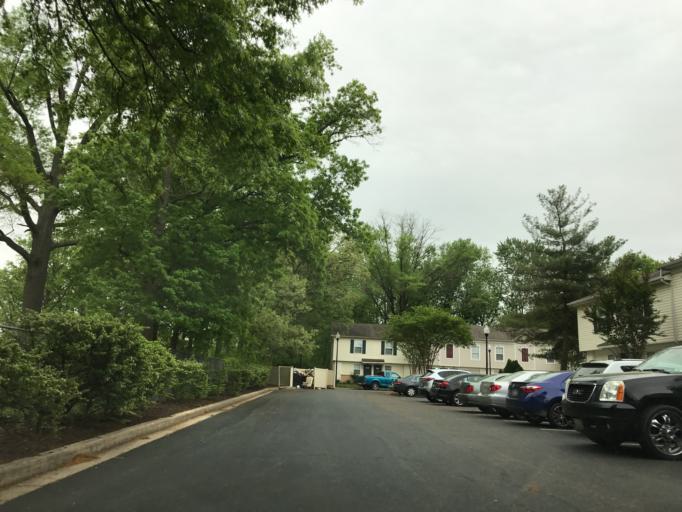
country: US
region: Maryland
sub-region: Baltimore County
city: Middle River
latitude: 39.3184
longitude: -76.4522
